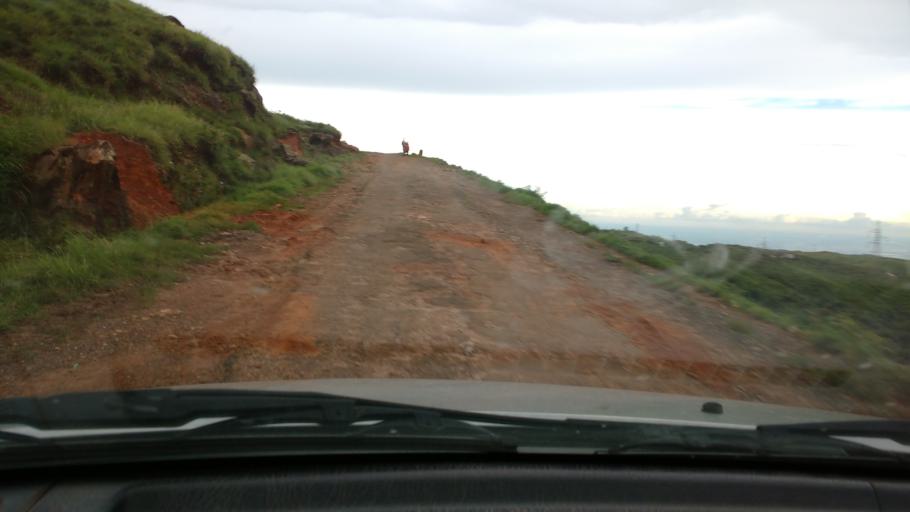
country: IN
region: Meghalaya
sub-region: East Khasi Hills
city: Cherrapunji
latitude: 25.2826
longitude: 91.7107
